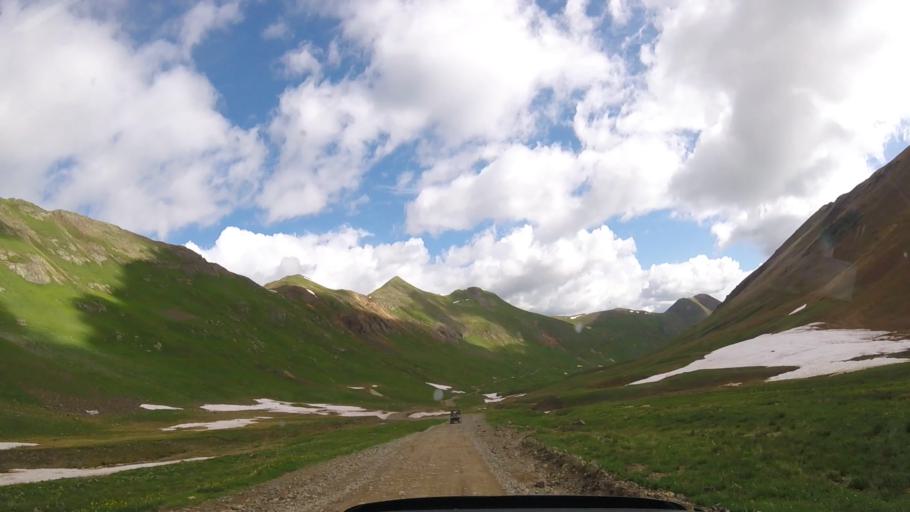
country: US
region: Colorado
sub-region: San Juan County
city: Silverton
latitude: 37.9172
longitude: -107.6129
